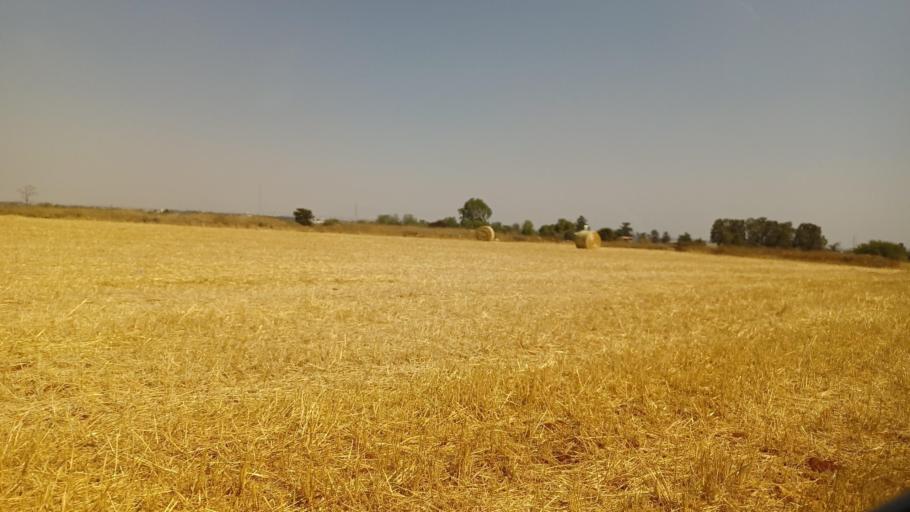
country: CY
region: Ammochostos
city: Frenaros
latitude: 35.0642
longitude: 33.9111
